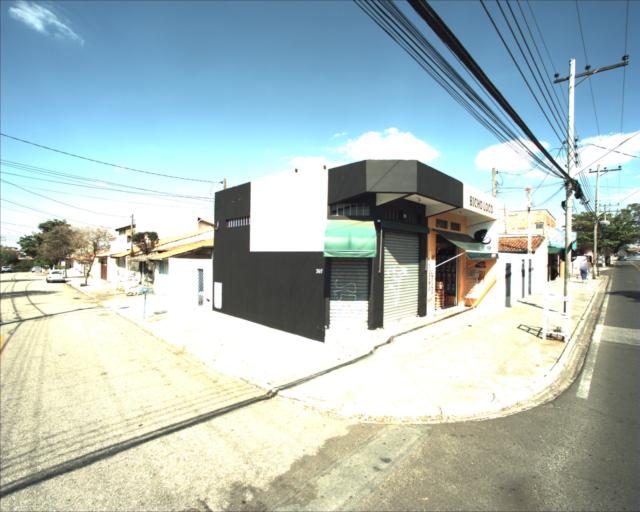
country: BR
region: Sao Paulo
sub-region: Sorocaba
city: Sorocaba
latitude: -23.5015
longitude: -47.5169
